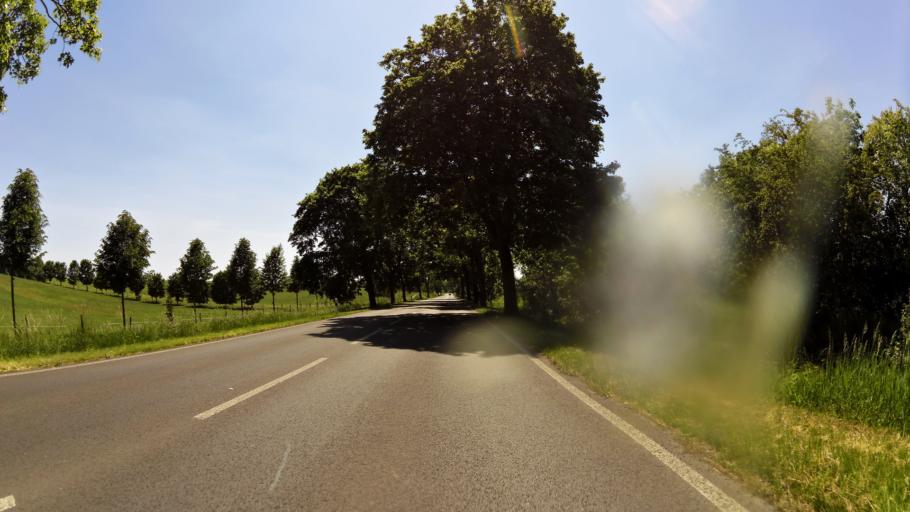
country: DE
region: Brandenburg
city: Lebus
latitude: 52.4160
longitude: 14.5280
